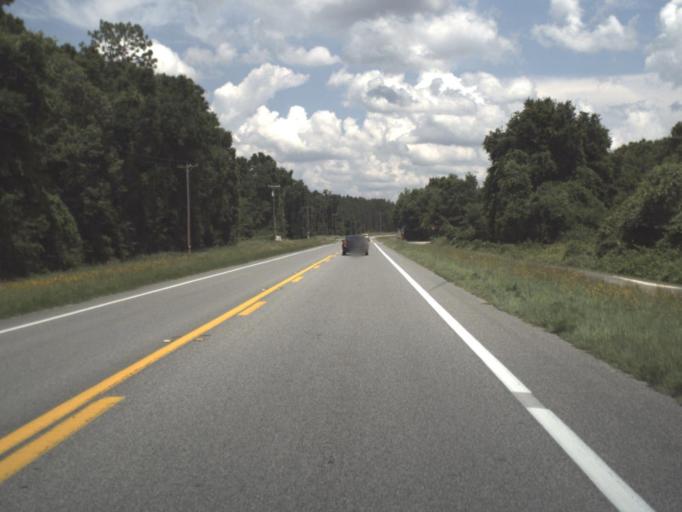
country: US
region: Florida
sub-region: Alachua County
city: High Springs
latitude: 29.9494
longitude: -82.7566
